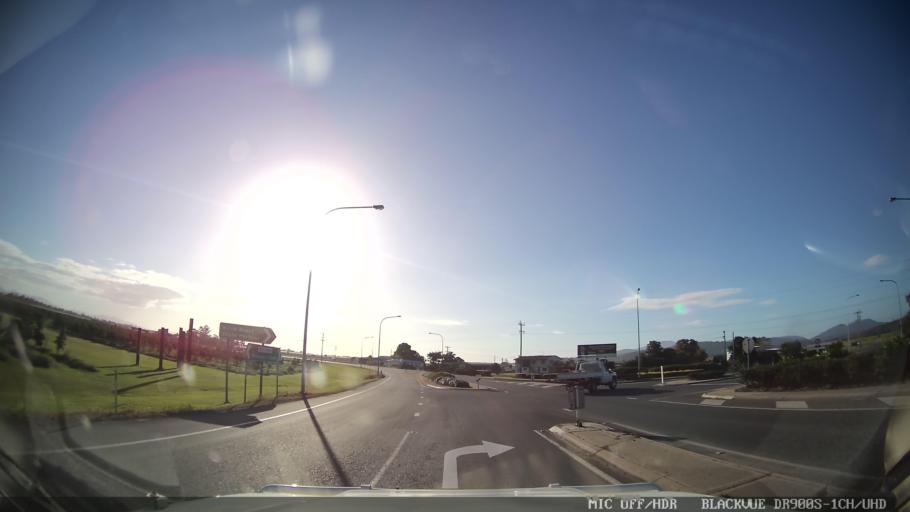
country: AU
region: Queensland
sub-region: Whitsunday
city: Proserpine
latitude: -20.3929
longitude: 148.5855
